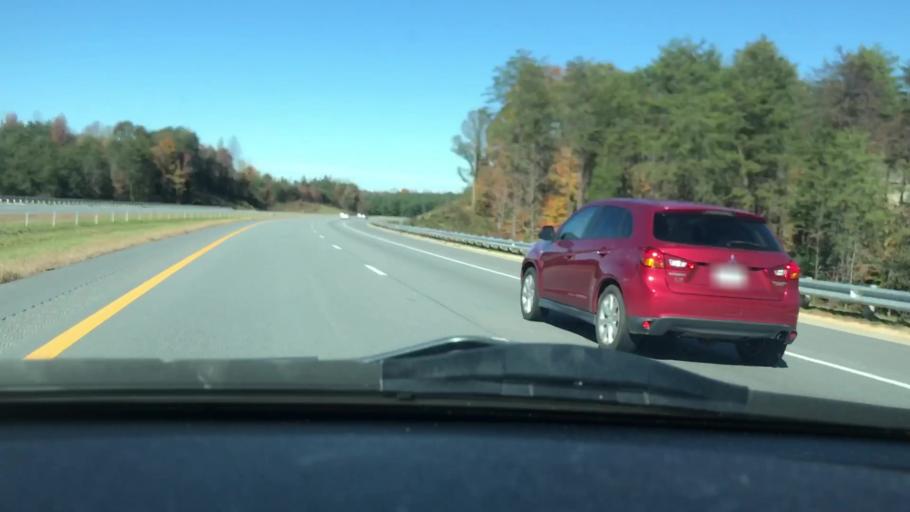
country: US
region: North Carolina
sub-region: Guilford County
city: Oak Ridge
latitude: 36.1567
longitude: -79.9593
